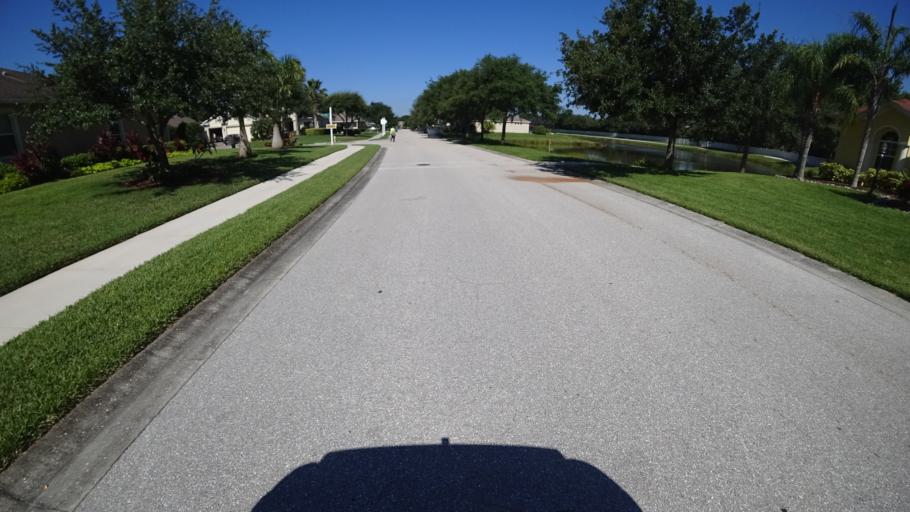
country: US
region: Florida
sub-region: Manatee County
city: Ellenton
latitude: 27.5682
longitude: -82.4367
